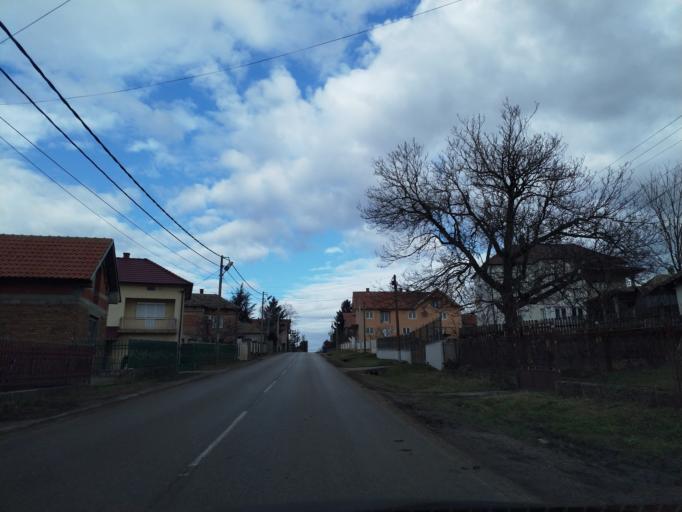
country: RS
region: Central Serbia
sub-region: Belgrade
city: Grocka
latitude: 44.6028
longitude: 20.7259
